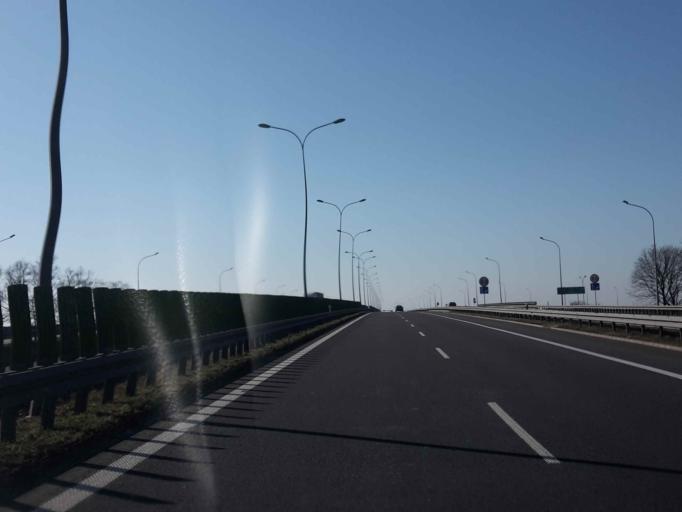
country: PL
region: Greater Poland Voivodeship
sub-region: Powiat poznanski
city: Kostrzyn
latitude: 52.3982
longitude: 17.2579
